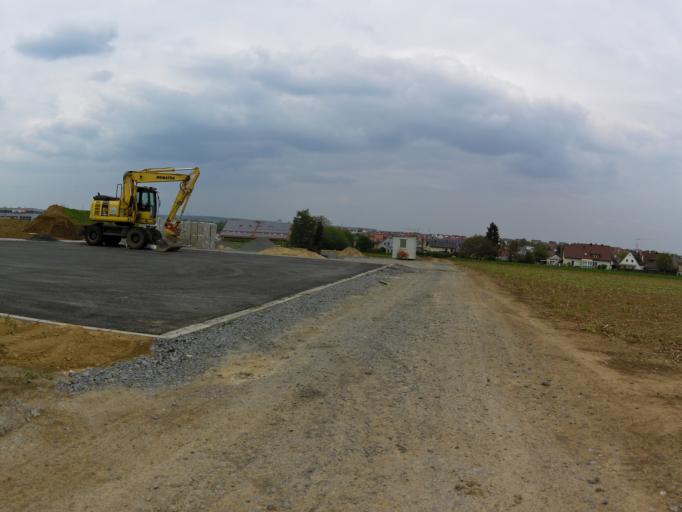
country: DE
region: Bavaria
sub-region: Regierungsbezirk Unterfranken
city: Unterpleichfeld
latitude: 49.8633
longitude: 10.0436
